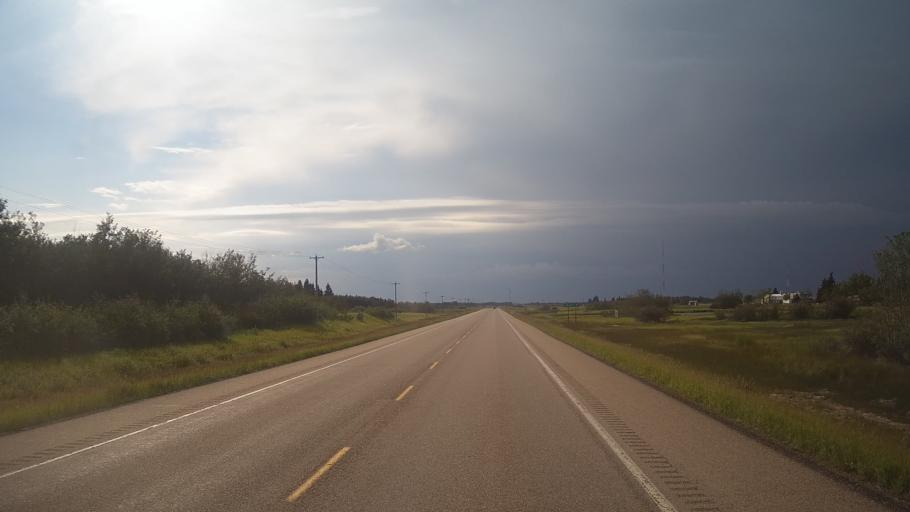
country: CA
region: Alberta
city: Viking
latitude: 53.1689
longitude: -112.0344
